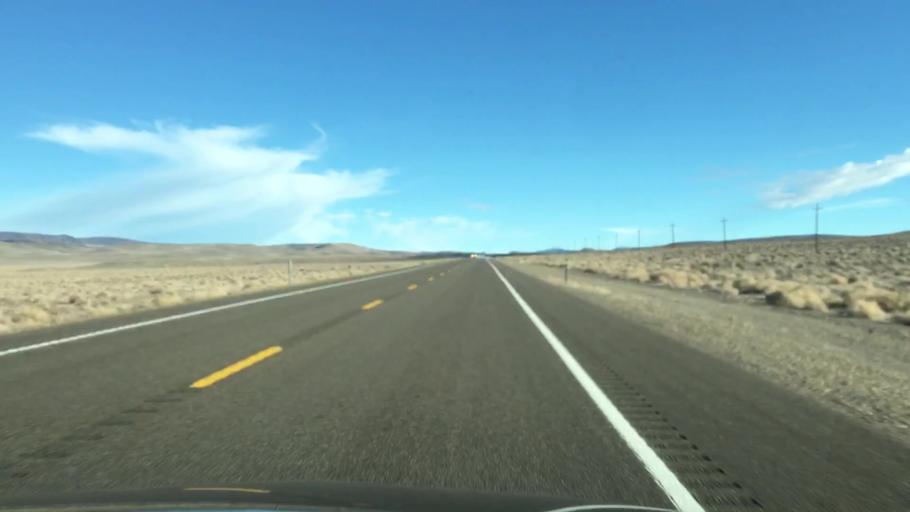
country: US
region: Nevada
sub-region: Mineral County
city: Hawthorne
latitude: 38.2518
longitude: -118.0747
